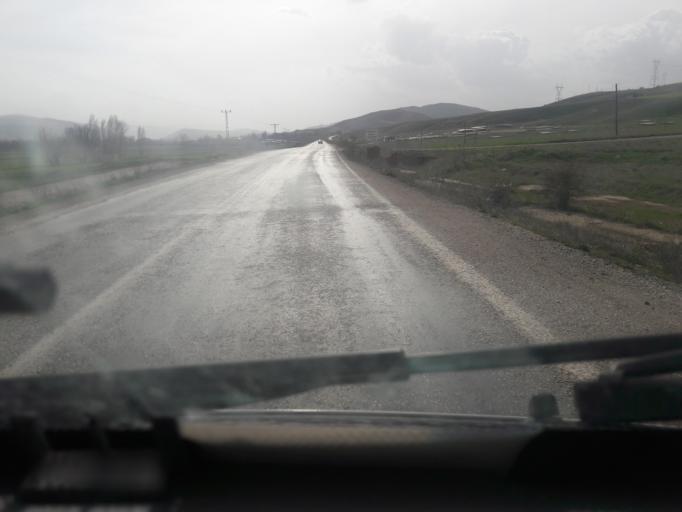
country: TR
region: Gumushane
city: Kelkit
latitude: 40.1433
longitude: 39.4098
